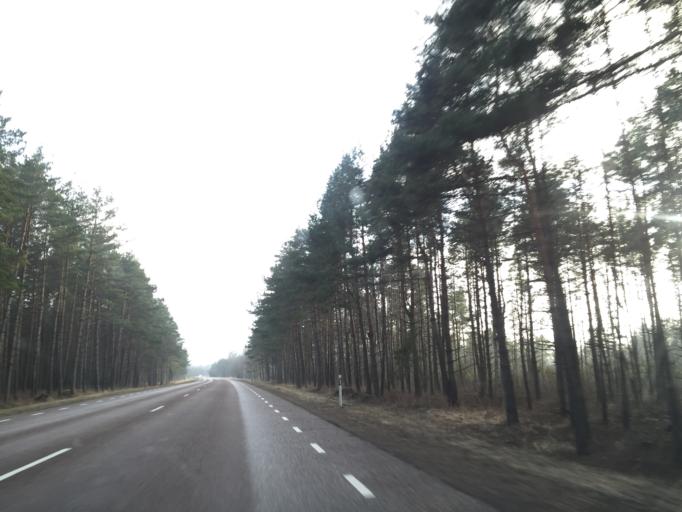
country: EE
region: Saare
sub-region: Kuressaare linn
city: Kuressaare
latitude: 58.3668
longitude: 22.7225
